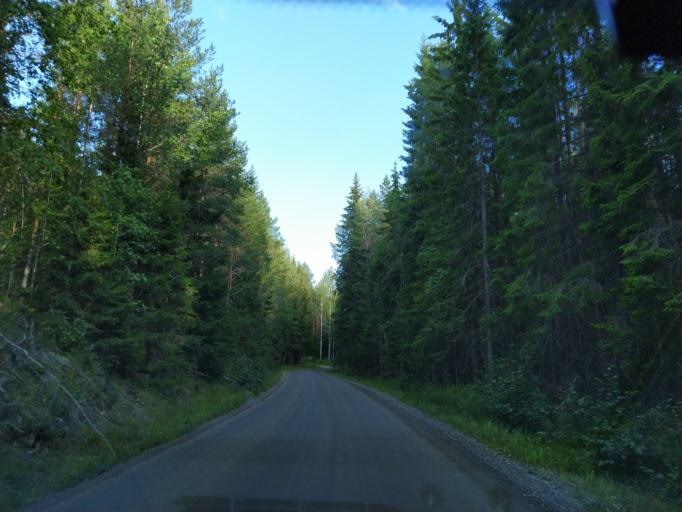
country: FI
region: Central Finland
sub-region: Jaemsae
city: Kuhmoinen
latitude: 61.6895
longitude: 24.9605
